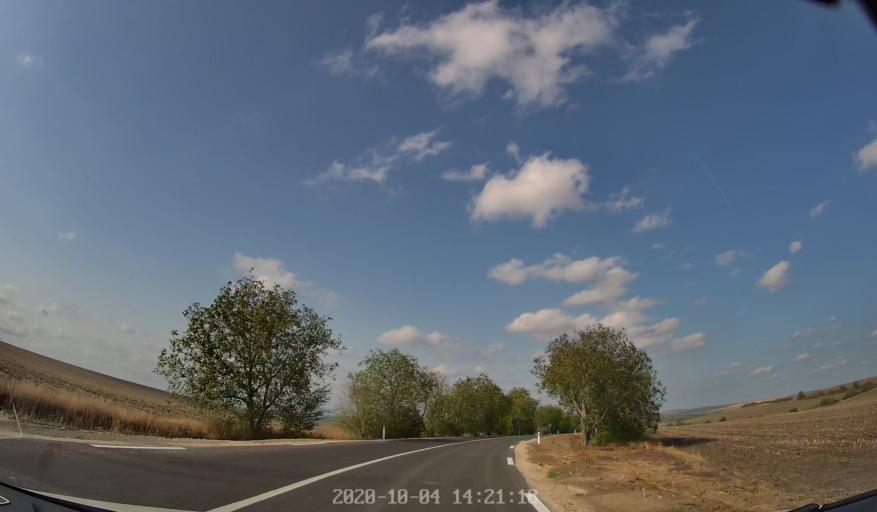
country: MD
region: Rezina
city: Saharna
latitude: 47.5834
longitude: 28.9563
